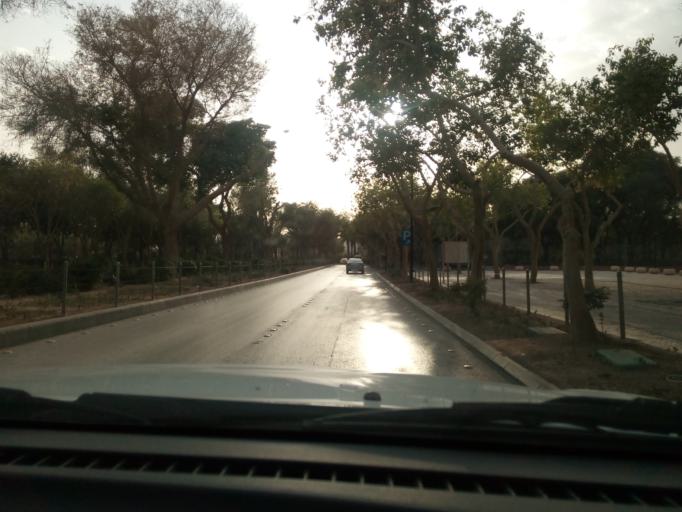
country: SA
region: Ar Riyad
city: Riyadh
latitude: 24.6453
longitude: 46.7092
